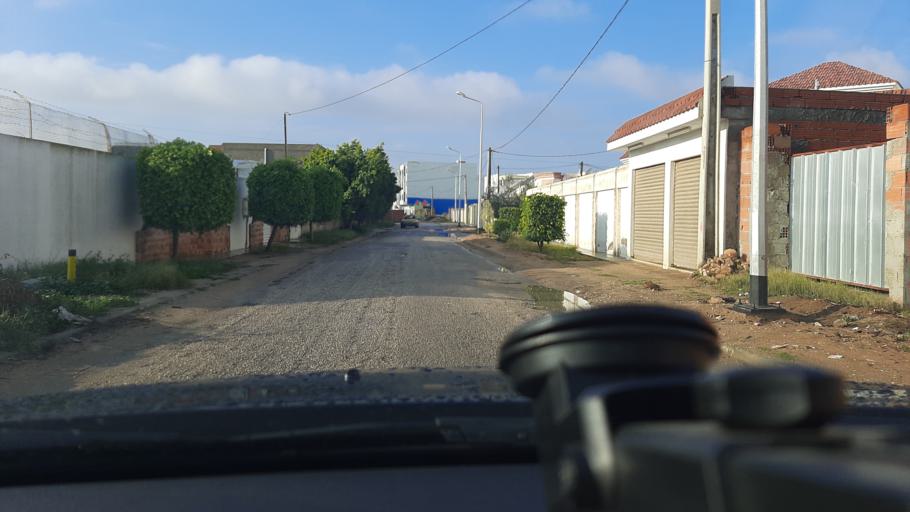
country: TN
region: Safaqis
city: Sfax
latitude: 34.7412
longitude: 10.7134
